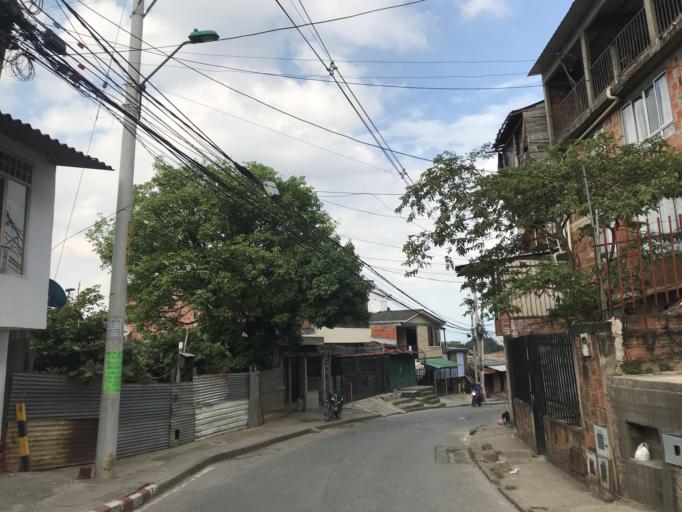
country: CO
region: Valle del Cauca
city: Cali
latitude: 3.3754
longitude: -76.5518
